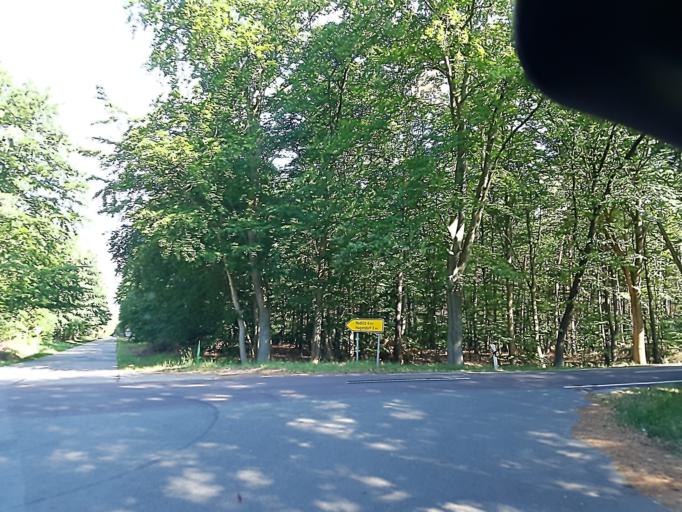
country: DE
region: Brandenburg
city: Gorzke
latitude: 52.0496
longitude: 12.2694
